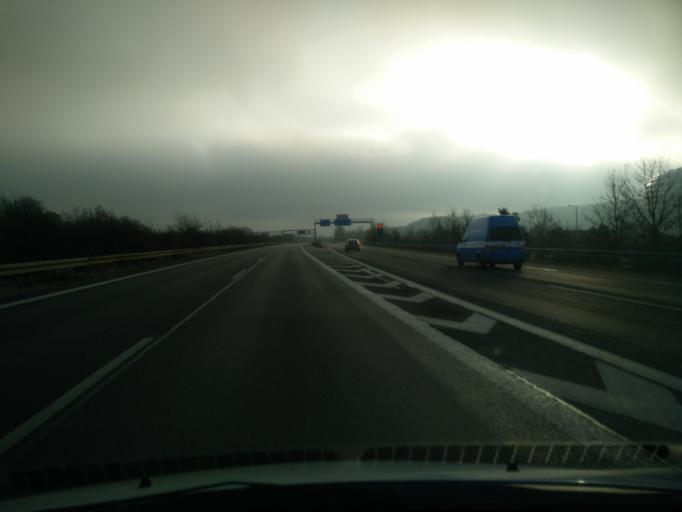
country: DE
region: Bavaria
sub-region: Upper Bavaria
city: Unterfoehring
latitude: 48.2238
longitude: 11.6226
